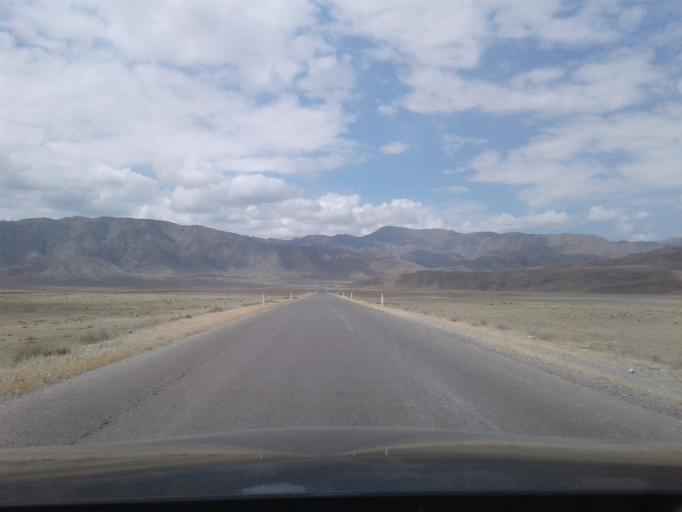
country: TM
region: Ahal
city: Baharly
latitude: 38.5234
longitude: 57.1422
